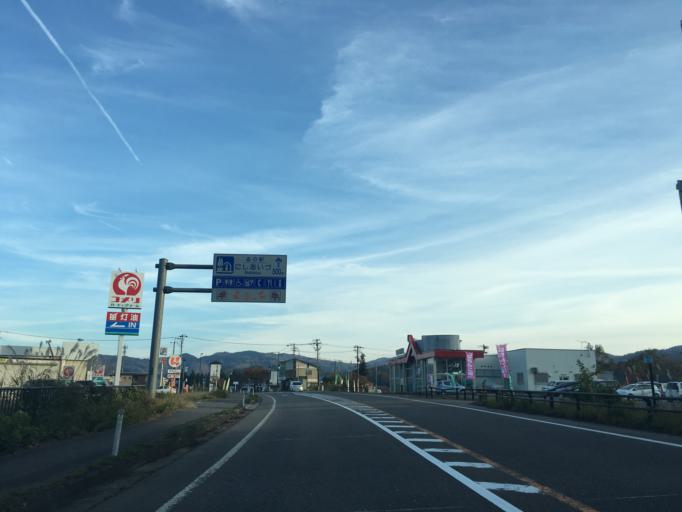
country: JP
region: Fukushima
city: Kitakata
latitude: 37.5890
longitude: 139.6340
